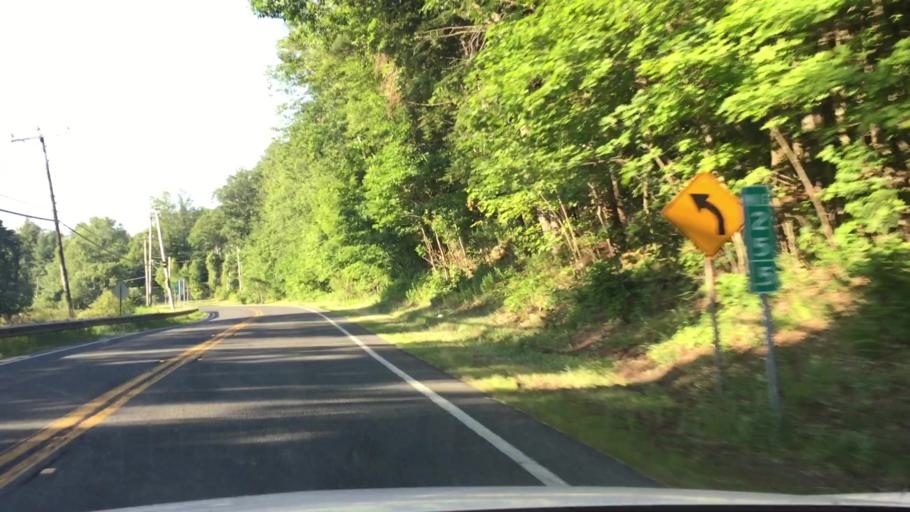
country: US
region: Massachusetts
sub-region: Berkshire County
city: Becket
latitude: 42.2673
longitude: -73.1367
